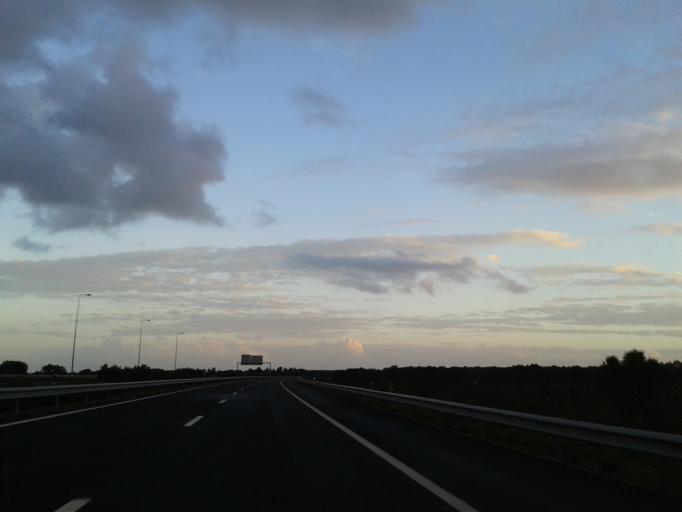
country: PT
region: Santarem
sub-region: Benavente
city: Poceirao
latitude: 38.8353
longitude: -8.7241
